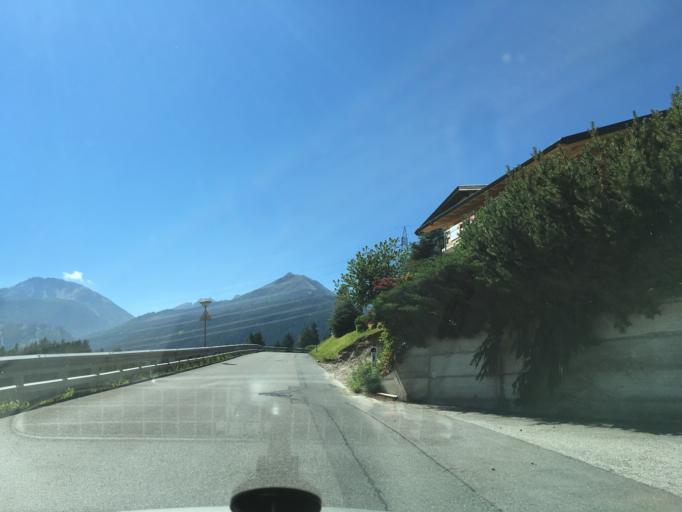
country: AT
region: Tyrol
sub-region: Politischer Bezirk Innsbruck Land
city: Oberperfuss
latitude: 47.2414
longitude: 11.2484
